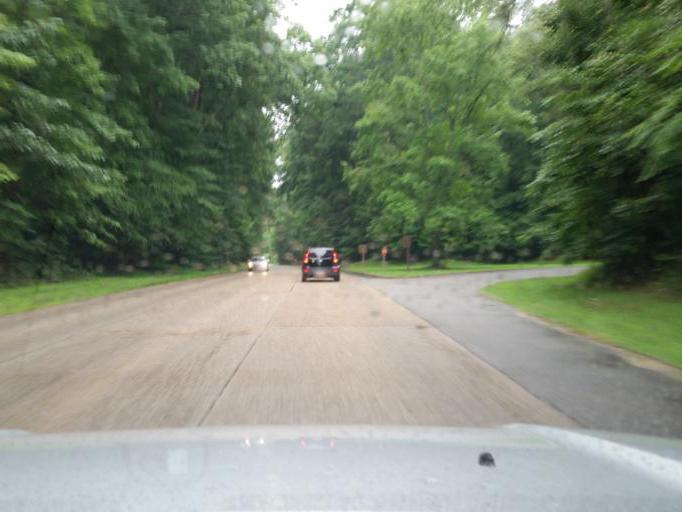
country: US
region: Virginia
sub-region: City of Williamsburg
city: Williamsburg
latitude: 37.2790
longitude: -76.6730
